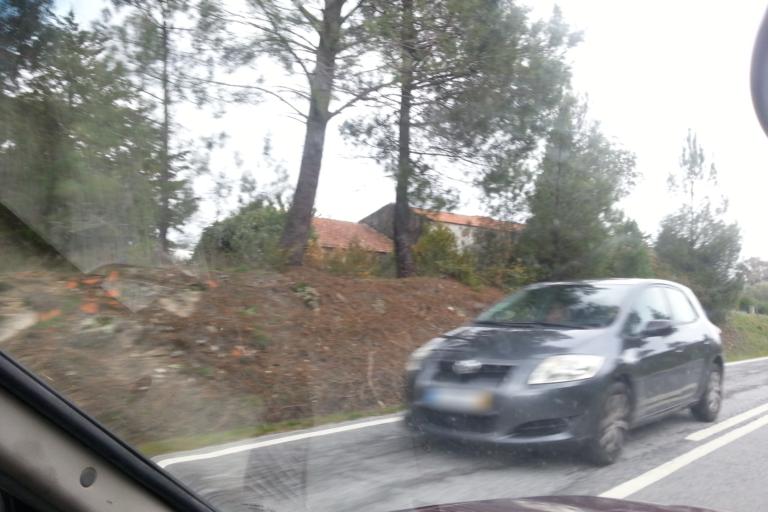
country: PT
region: Guarda
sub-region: Fornos de Algodres
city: Fornos de Algodres
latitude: 40.5351
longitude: -7.5534
